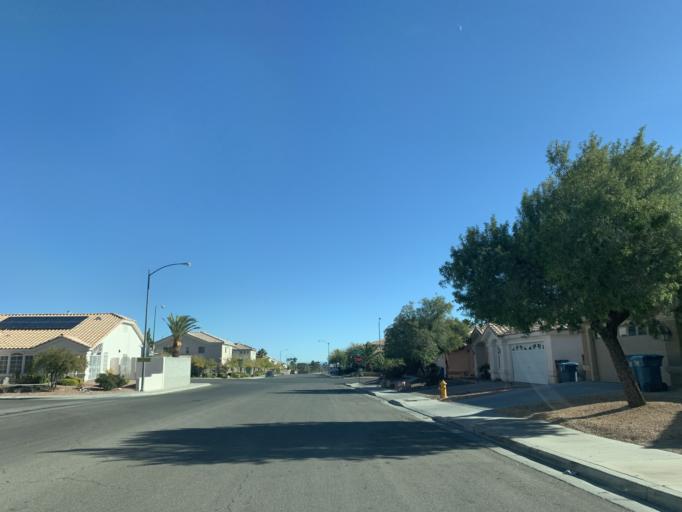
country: US
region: Nevada
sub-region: Clark County
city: Summerlin South
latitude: 36.1186
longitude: -115.2889
